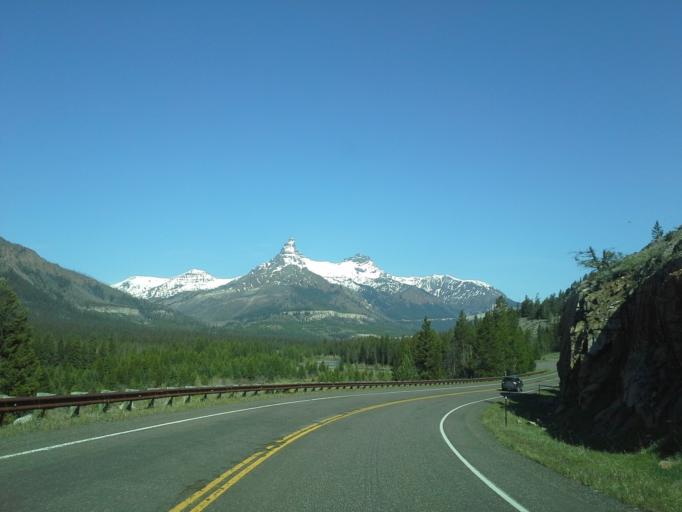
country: US
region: Montana
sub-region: Carbon County
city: Red Lodge
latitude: 44.9461
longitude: -109.7832
